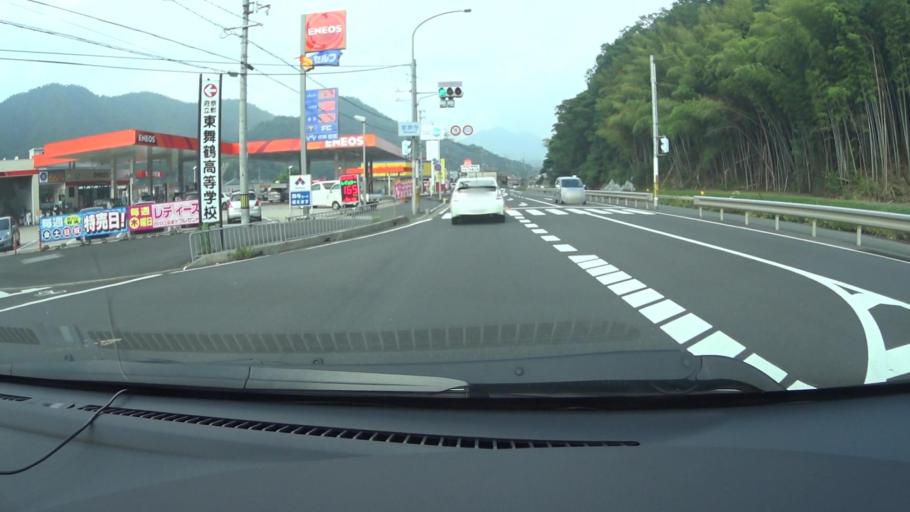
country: JP
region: Kyoto
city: Kameoka
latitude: 34.9949
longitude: 135.5788
